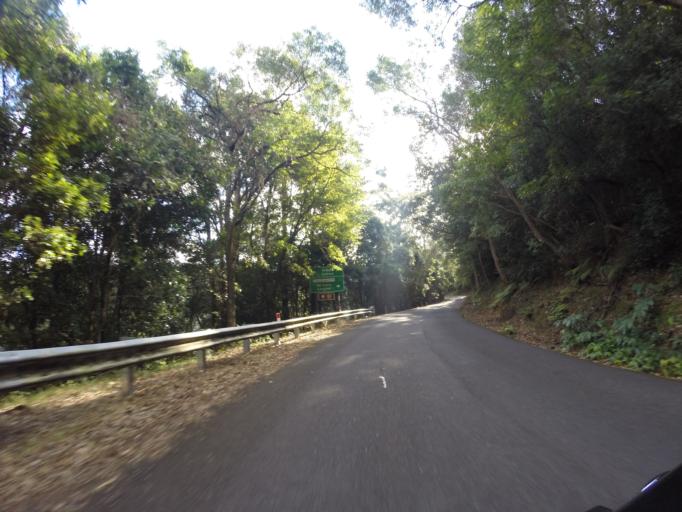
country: AU
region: New South Wales
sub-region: Wollongong
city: Mount Keira
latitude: -34.3978
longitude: 150.8506
